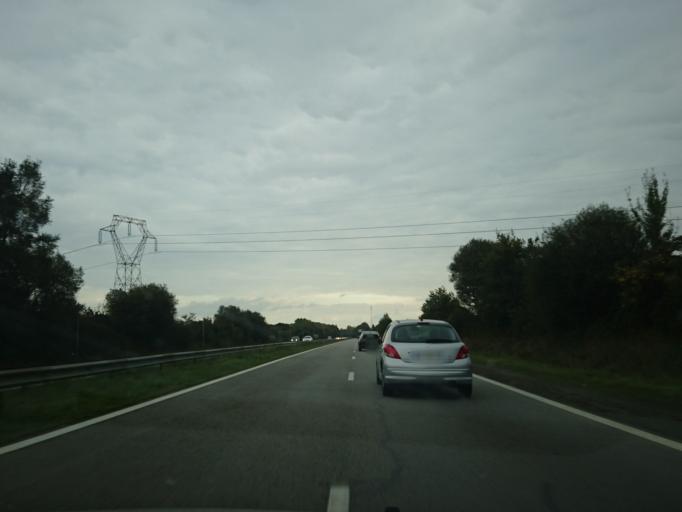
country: FR
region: Brittany
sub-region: Departement d'Ille-et-Vilaine
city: Quedillac
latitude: 48.2581
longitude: -2.1422
